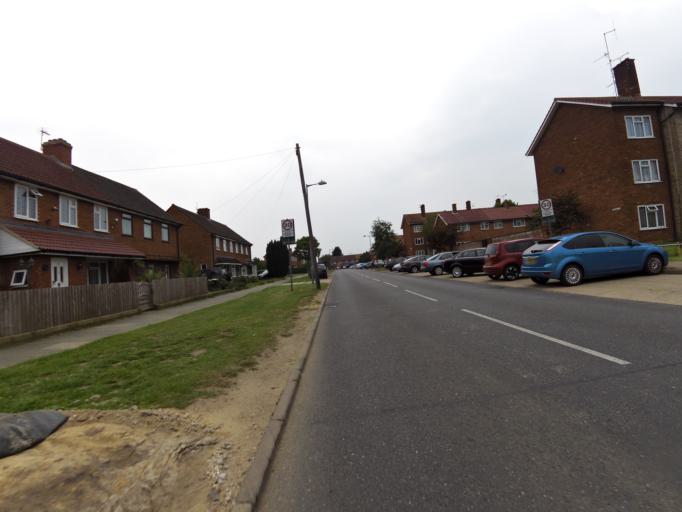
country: GB
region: England
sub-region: Suffolk
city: Ipswich
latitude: 52.0845
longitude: 1.1364
